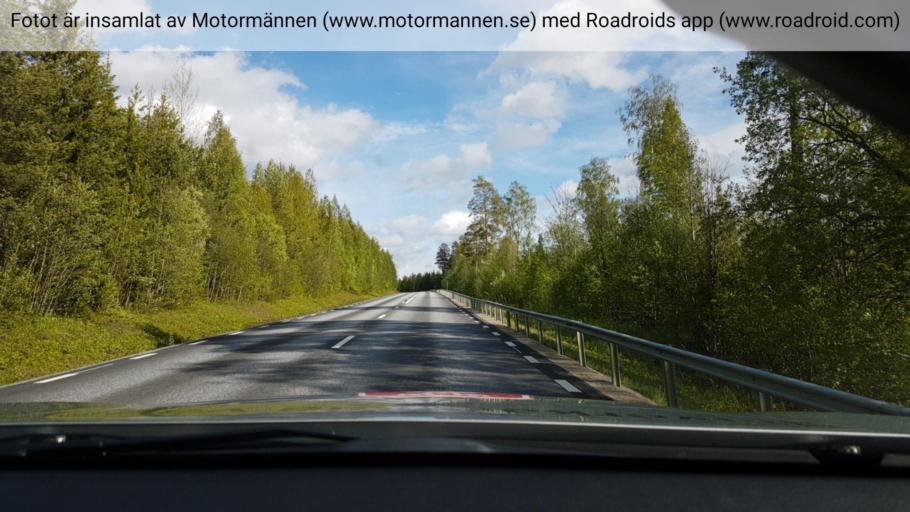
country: SE
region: Vaesterbotten
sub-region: Bjurholms Kommun
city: Bjurholm
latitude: 63.9169
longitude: 19.1527
